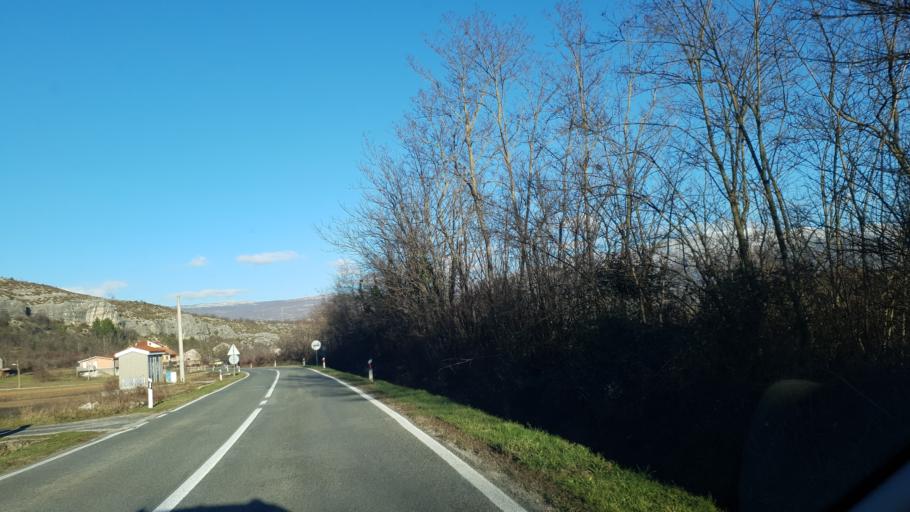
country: HR
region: Splitsko-Dalmatinska
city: Sinj
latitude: 43.7174
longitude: 16.6665
